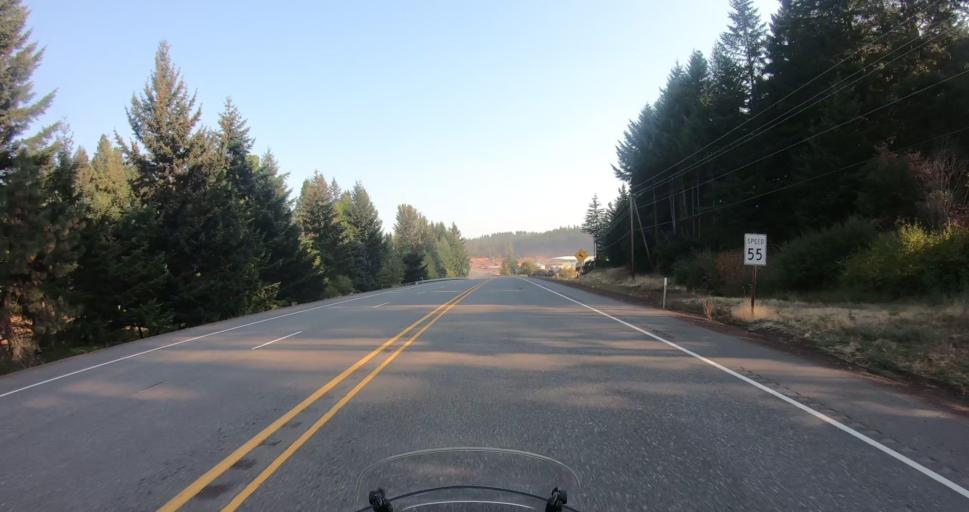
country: US
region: Oregon
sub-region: Hood River County
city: Odell
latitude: 45.5812
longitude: -121.5520
